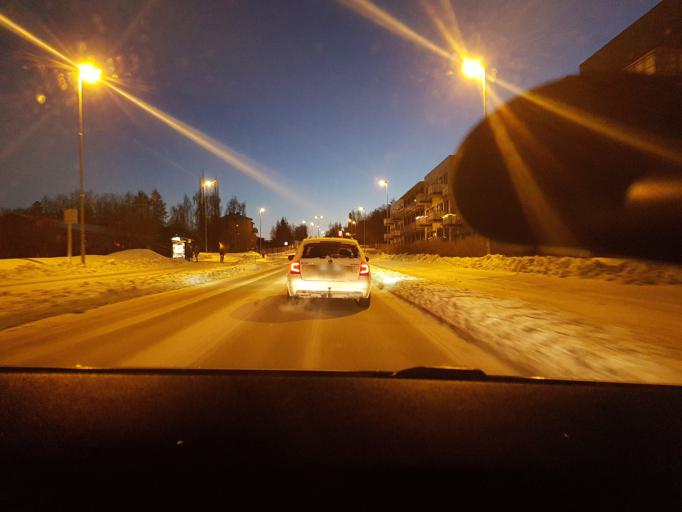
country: NO
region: Sor-Trondelag
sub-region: Trondheim
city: Trondheim
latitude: 63.4050
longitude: 10.3587
